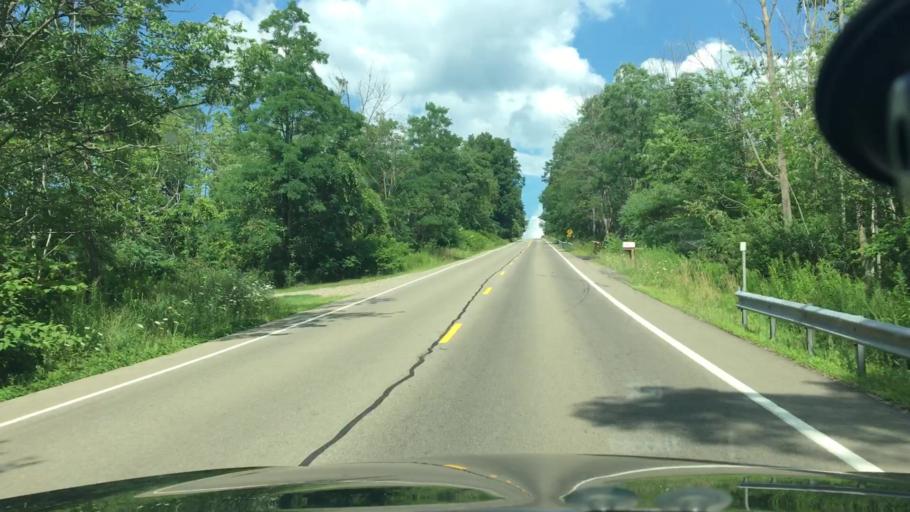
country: US
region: New York
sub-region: Chautauqua County
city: Lakewood
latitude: 42.1785
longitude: -79.3589
